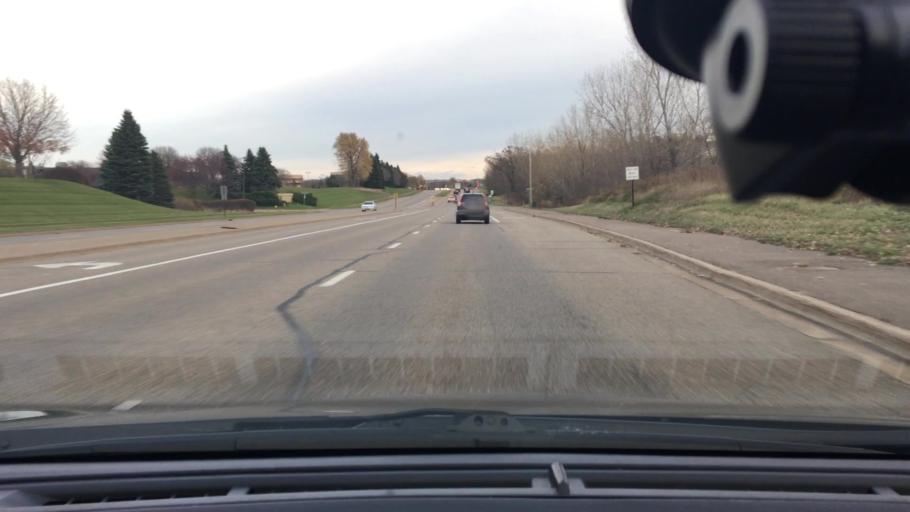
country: US
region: Minnesota
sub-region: Hennepin County
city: New Hope
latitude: 45.0585
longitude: -93.4157
